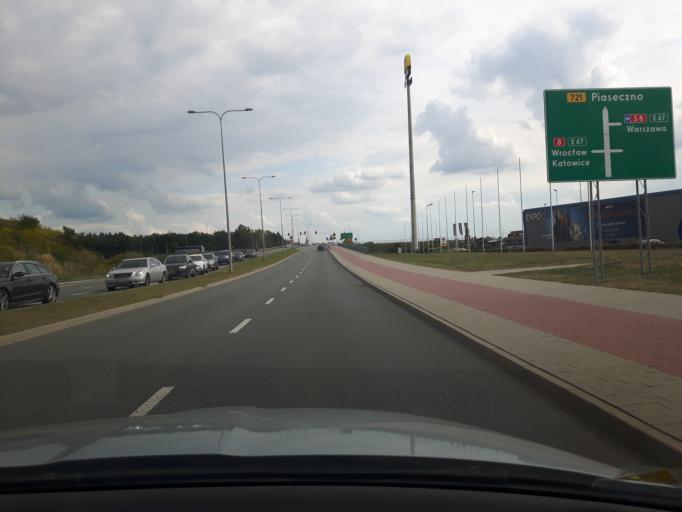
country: PL
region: Masovian Voivodeship
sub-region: Powiat pruszkowski
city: Nadarzyn
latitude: 52.1093
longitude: 20.8344
